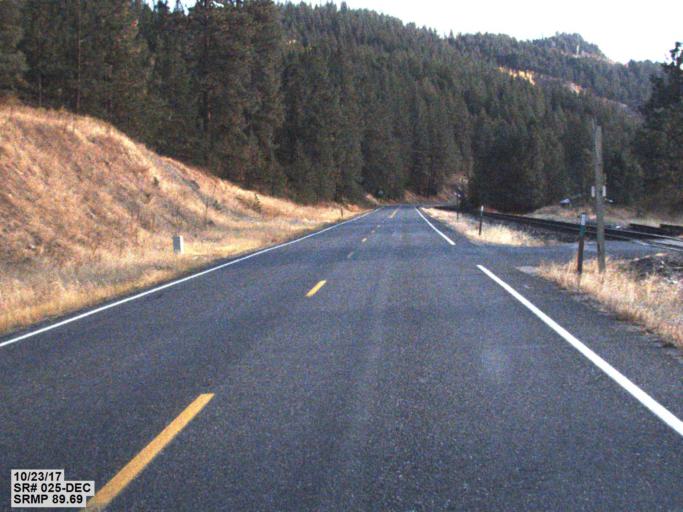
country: US
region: Washington
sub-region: Stevens County
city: Kettle Falls
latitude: 48.6938
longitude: -118.0126
